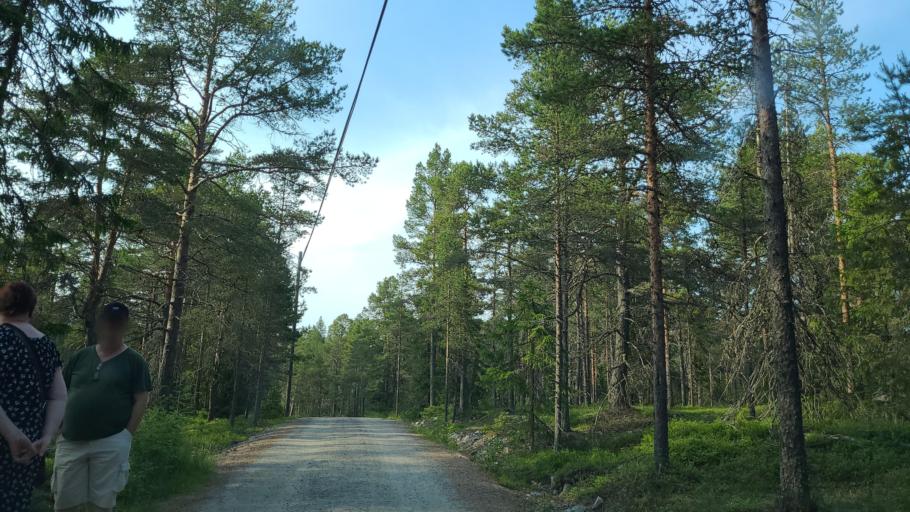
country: SE
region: Vaesterbotten
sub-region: Skelleftea Kommun
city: Skelleftehamn
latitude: 64.4769
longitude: 21.5754
